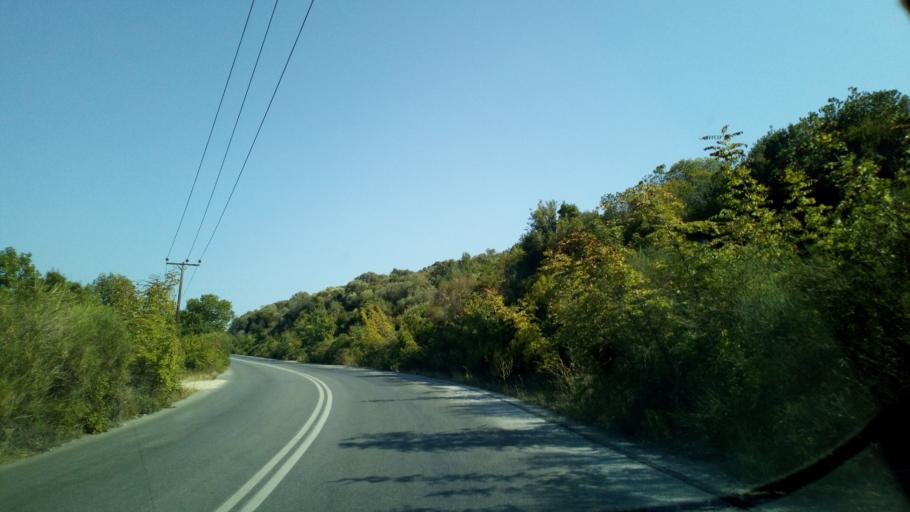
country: GR
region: Central Macedonia
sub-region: Nomos Thessalonikis
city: Stavros
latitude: 40.6231
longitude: 23.7683
